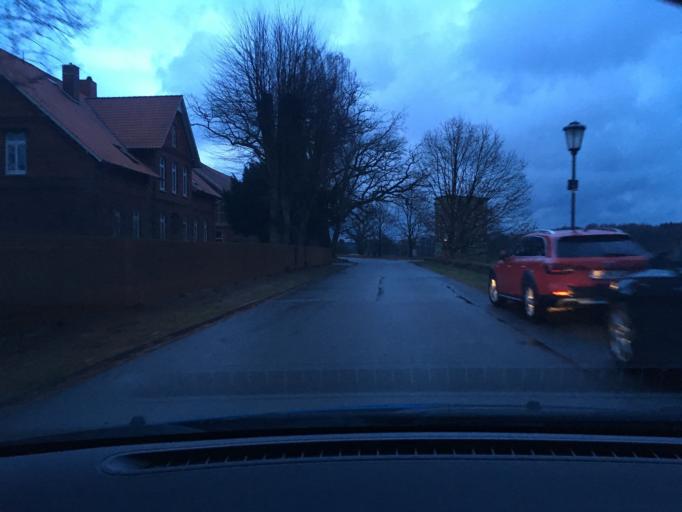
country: DE
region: Lower Saxony
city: Betzendorf
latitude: 53.1396
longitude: 10.3130
